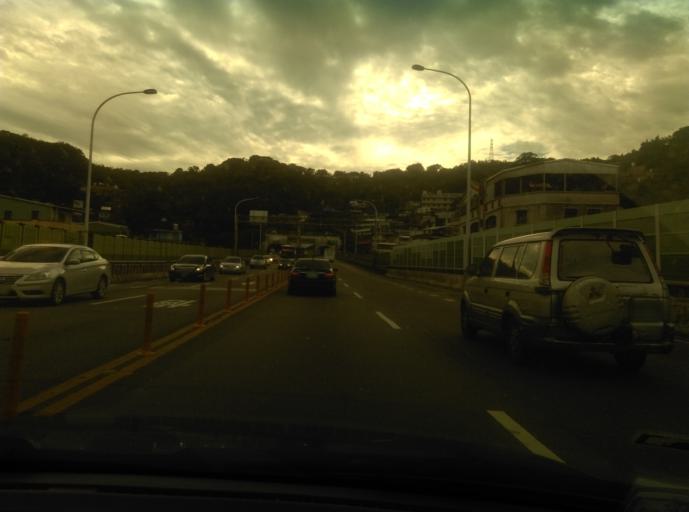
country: TW
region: Taiwan
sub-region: Keelung
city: Keelung
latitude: 25.1251
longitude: 121.7371
